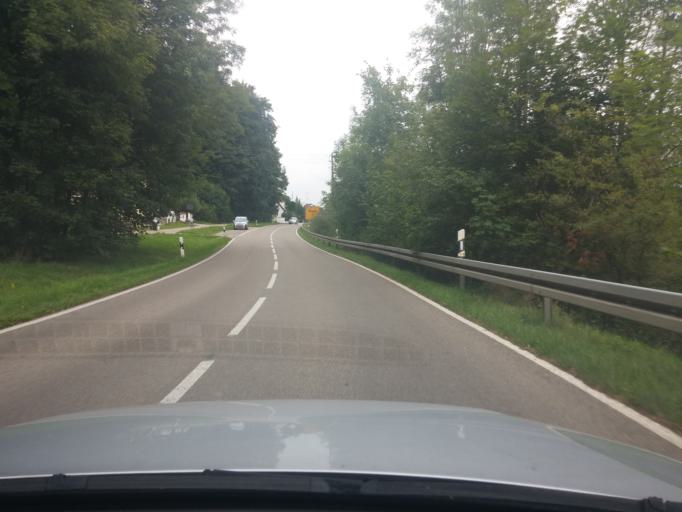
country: DE
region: Bavaria
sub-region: Swabia
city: Memmingen
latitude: 47.9564
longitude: 10.1827
